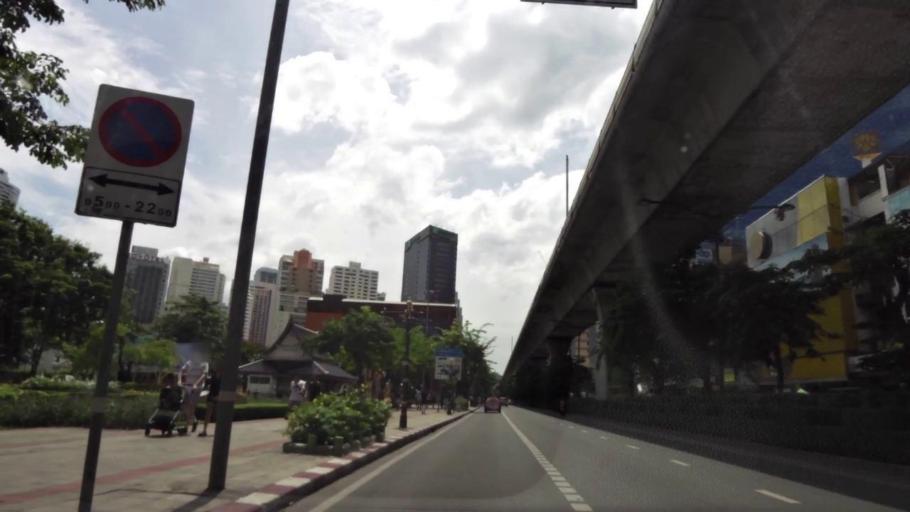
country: TH
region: Bangkok
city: Khlong Toei
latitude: 13.7313
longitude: 100.5683
